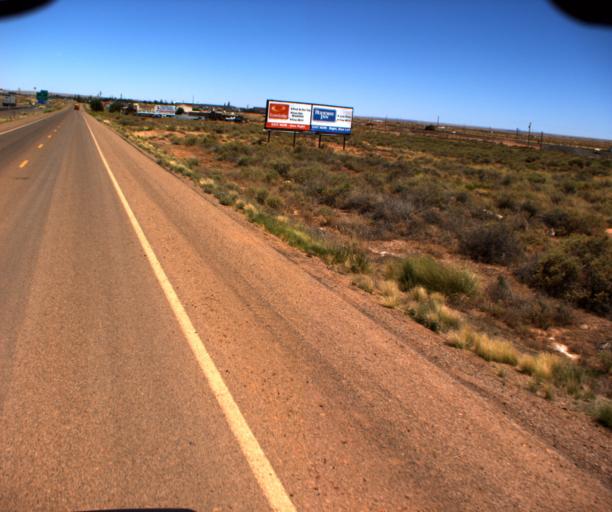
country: US
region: Arizona
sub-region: Coconino County
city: LeChee
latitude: 35.0397
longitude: -110.7404
